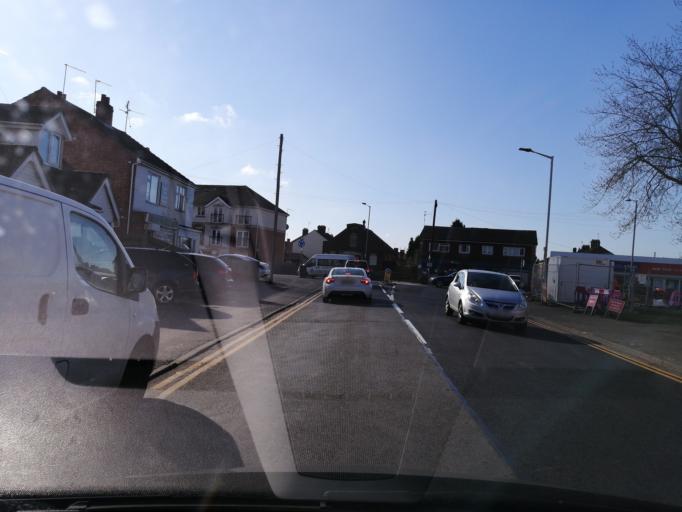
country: GB
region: England
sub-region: Peterborough
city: Peterborough
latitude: 52.5963
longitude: -0.2459
